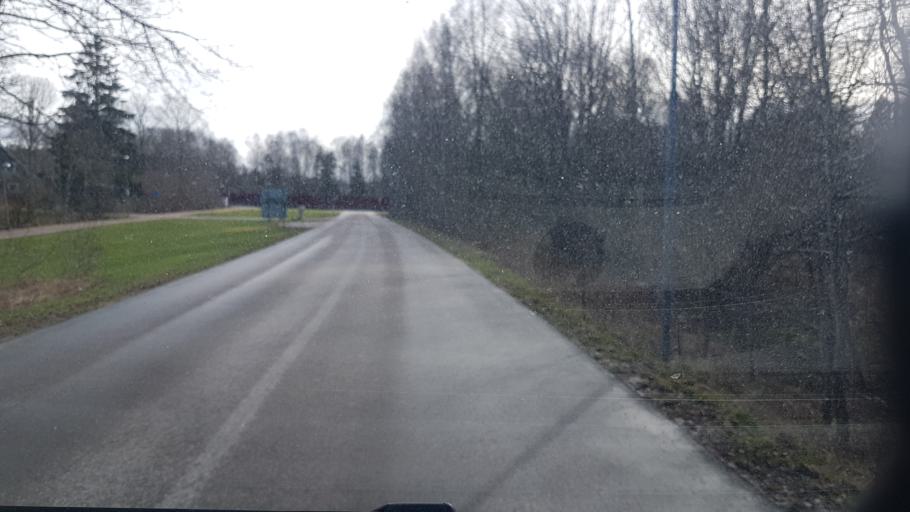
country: SE
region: Vaestra Goetaland
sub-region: Lerums Kommun
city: Stenkullen
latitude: 57.8068
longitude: 12.3743
